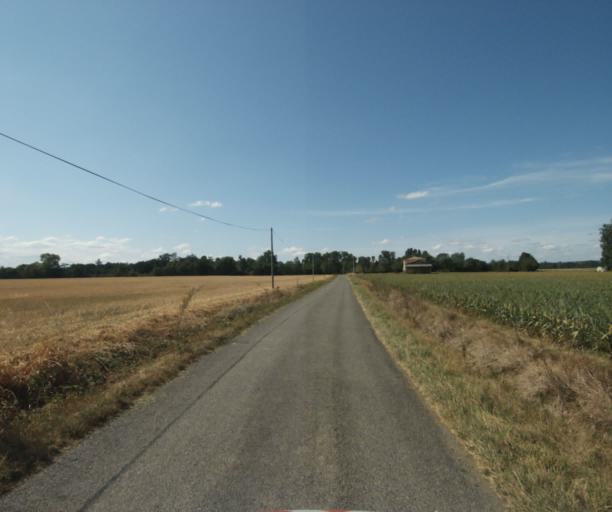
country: FR
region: Midi-Pyrenees
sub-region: Departement de la Haute-Garonne
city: Revel
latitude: 43.4790
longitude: 1.9743
